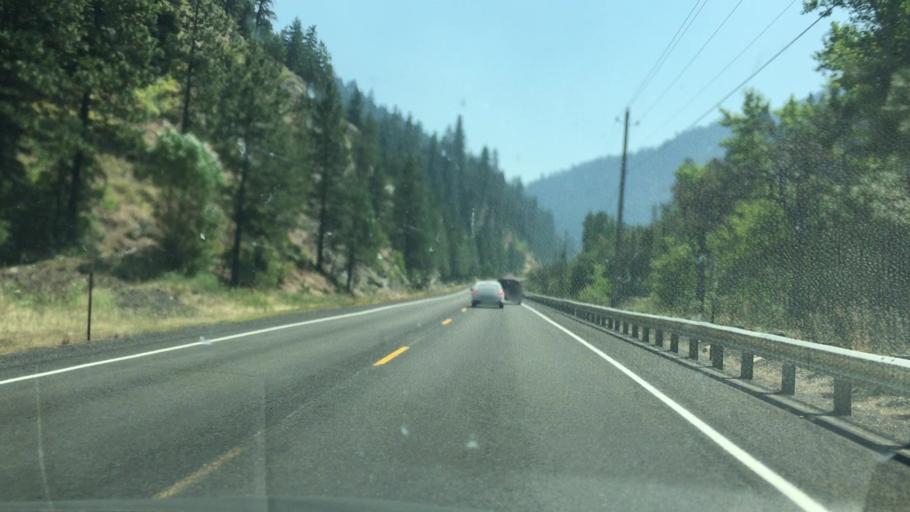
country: US
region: Idaho
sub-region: Valley County
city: McCall
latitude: 45.1621
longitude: -116.3004
